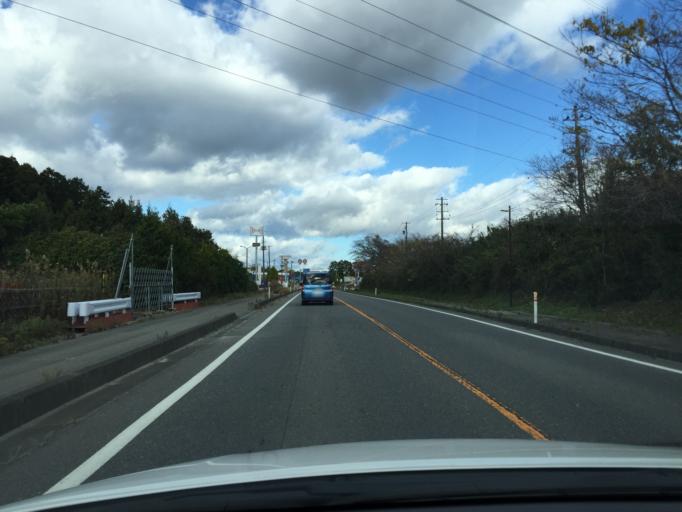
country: JP
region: Fukushima
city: Namie
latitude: 37.4002
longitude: 141.0014
